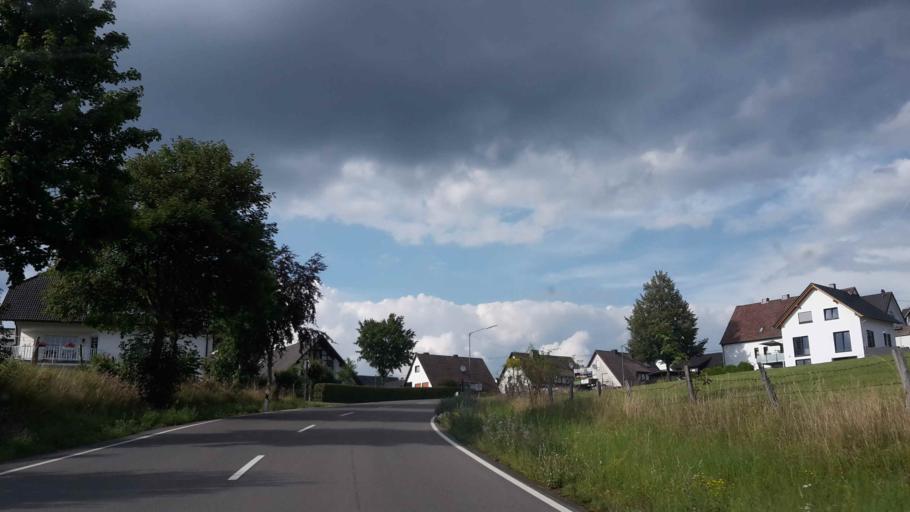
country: DE
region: North Rhine-Westphalia
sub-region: Regierungsbezirk Arnsberg
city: Lennestadt
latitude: 51.1368
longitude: 8.0826
